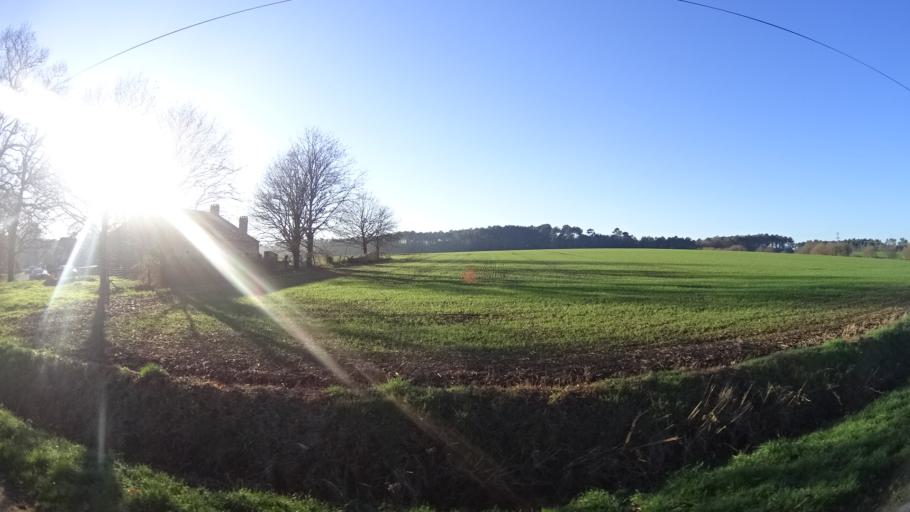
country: FR
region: Brittany
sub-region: Departement du Morbihan
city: Saint-Jacut-les-Pins
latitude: 47.6708
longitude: -2.1809
